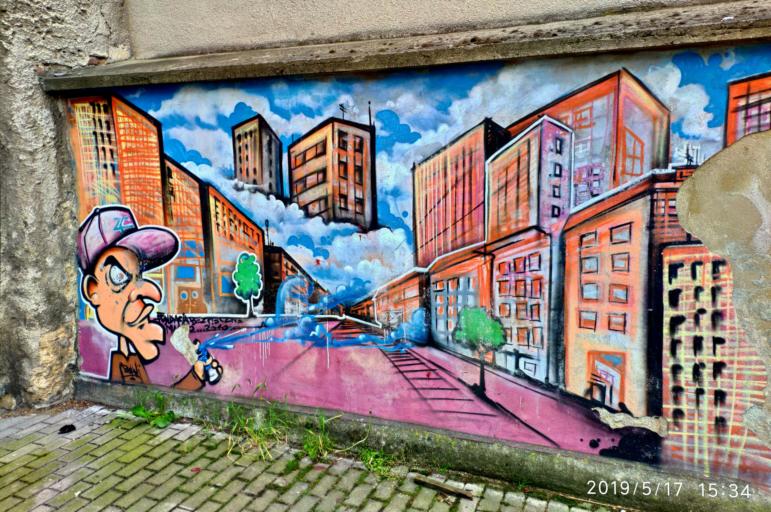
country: PL
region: Lubusz
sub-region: Zielona Gora
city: Zielona Gora
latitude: 51.9375
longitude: 15.4976
